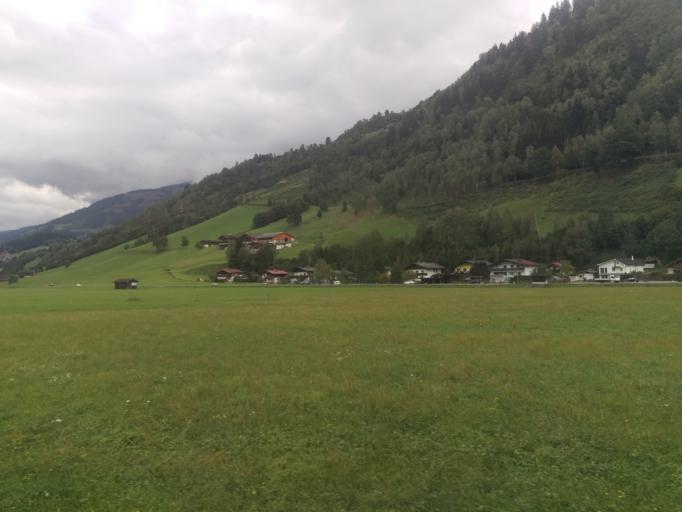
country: AT
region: Salzburg
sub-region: Politischer Bezirk Zell am See
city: Niedernsill
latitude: 47.2837
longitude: 12.6712
